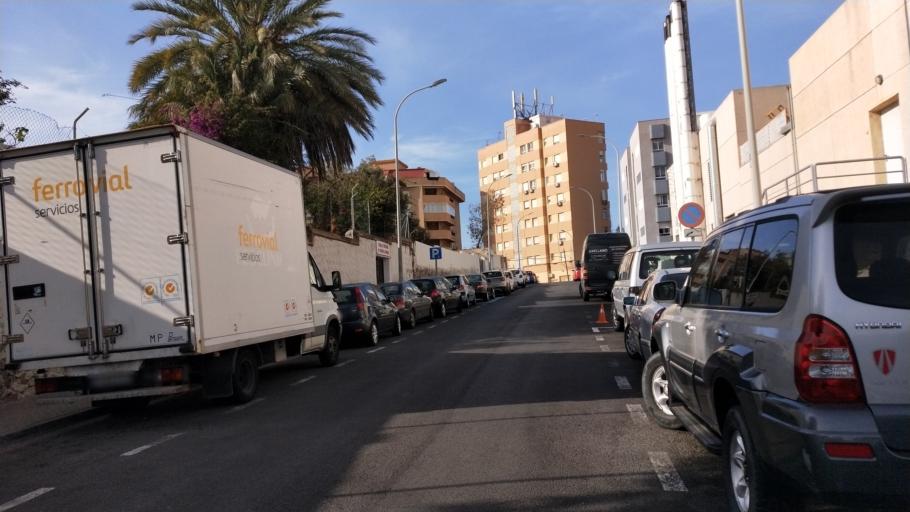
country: ES
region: Melilla
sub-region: Melilla
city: Melilla
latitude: 35.2863
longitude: -2.9482
